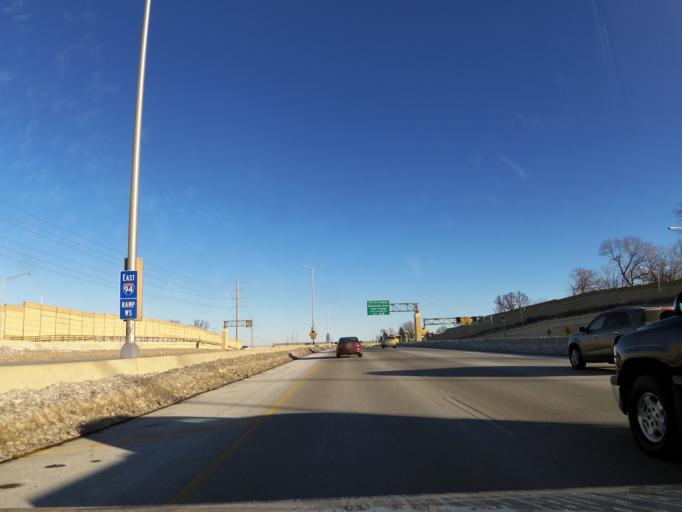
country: US
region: Wisconsin
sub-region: Milwaukee County
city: Greendale
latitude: 42.9626
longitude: -87.9441
